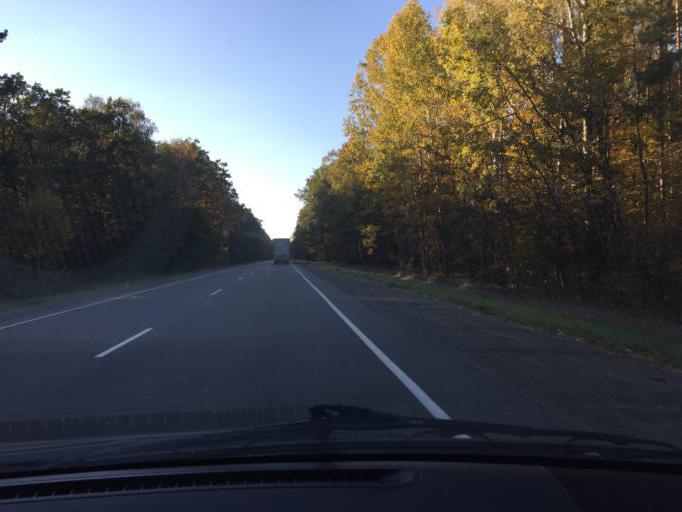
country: BY
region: Brest
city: Horad Luninyets
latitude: 52.2842
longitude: 26.8082
